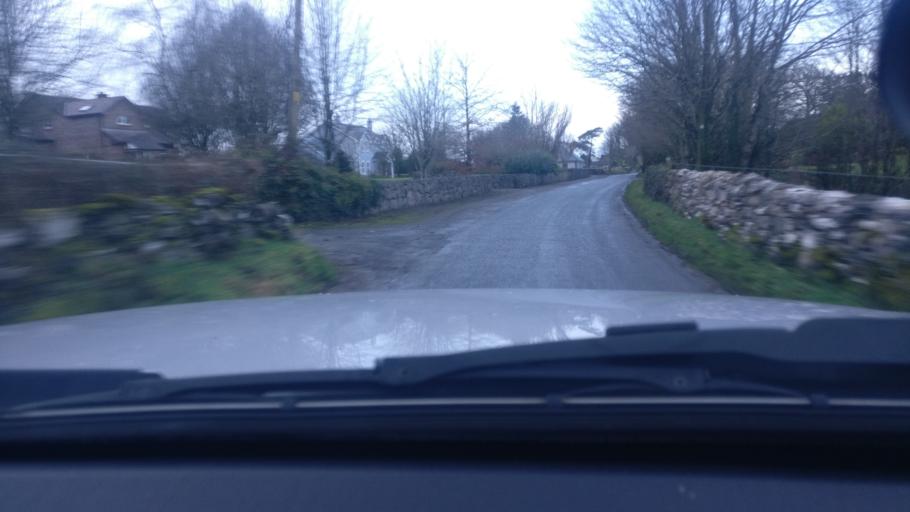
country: IE
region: Connaught
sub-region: County Galway
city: Loughrea
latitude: 53.1808
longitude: -8.5973
